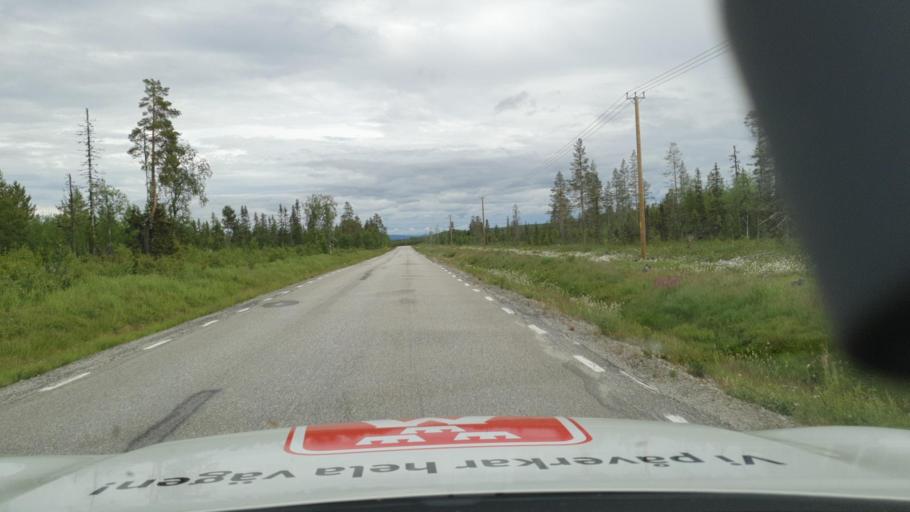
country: SE
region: Vaesterbotten
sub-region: Lycksele Kommun
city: Soderfors
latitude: 64.3848
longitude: 18.0152
